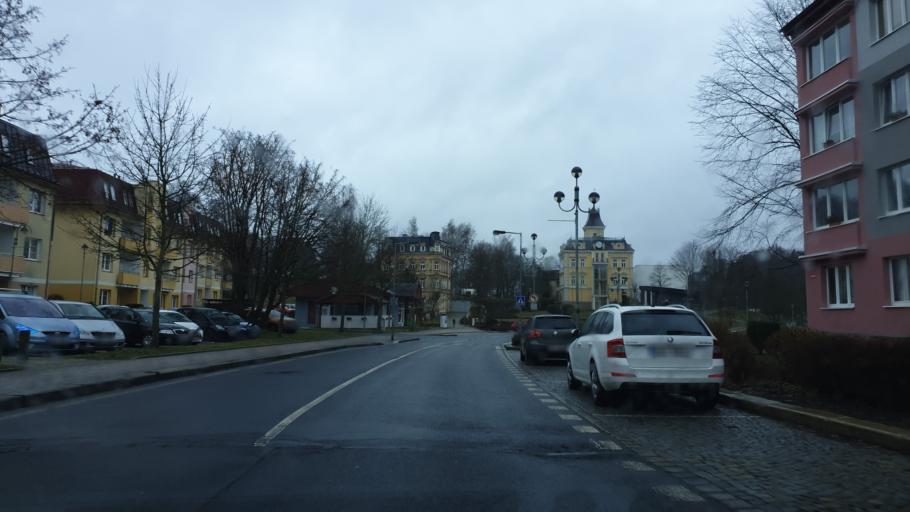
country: CZ
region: Karlovarsky
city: As
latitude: 50.2240
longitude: 12.1865
